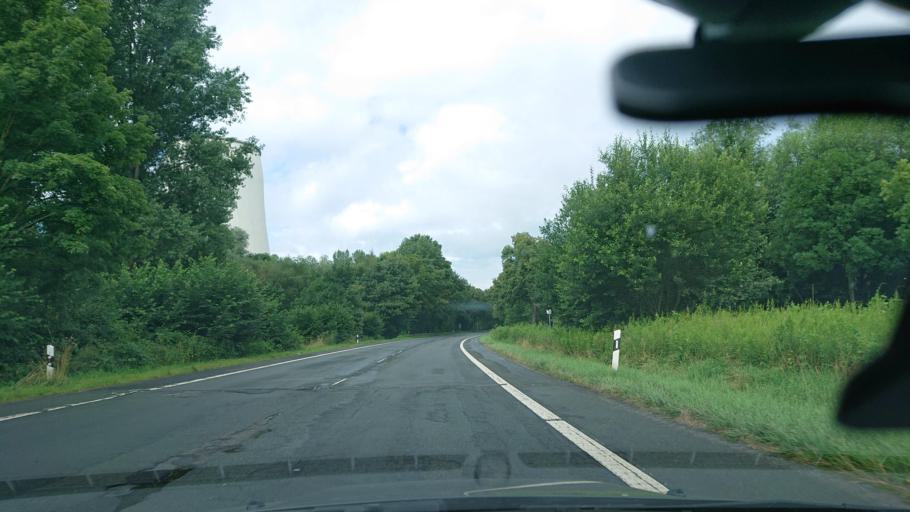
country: DE
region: North Rhine-Westphalia
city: Werne
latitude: 51.6407
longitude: 7.6228
